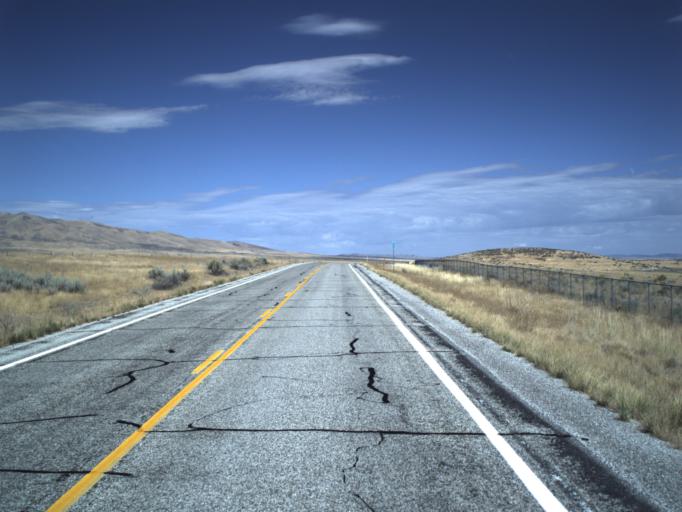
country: US
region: Utah
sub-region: Box Elder County
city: Tremonton
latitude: 41.7089
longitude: -112.4514
